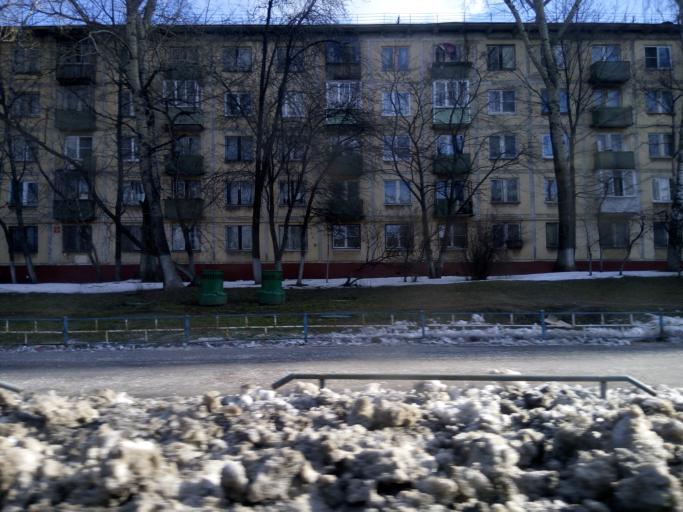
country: RU
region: Moscow
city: Kotlovka
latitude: 55.6713
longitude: 37.5876
